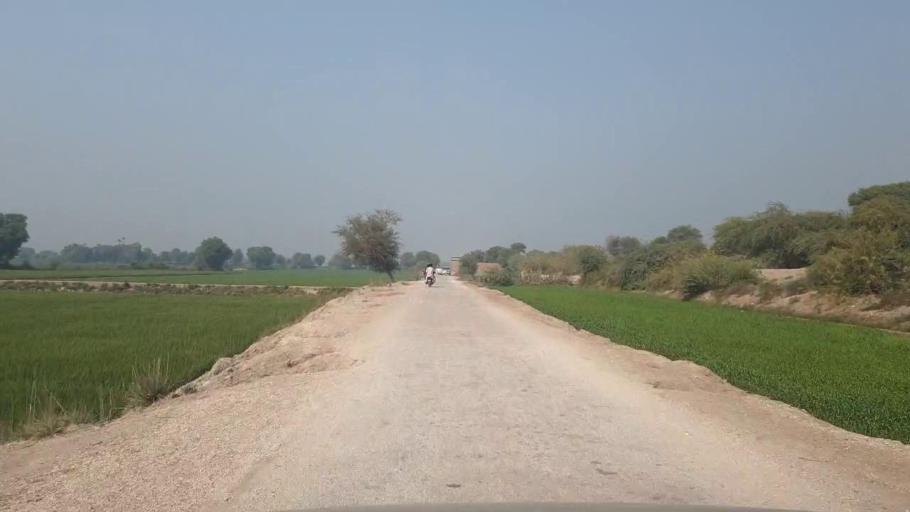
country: PK
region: Sindh
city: Hala
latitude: 25.8175
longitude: 68.4103
